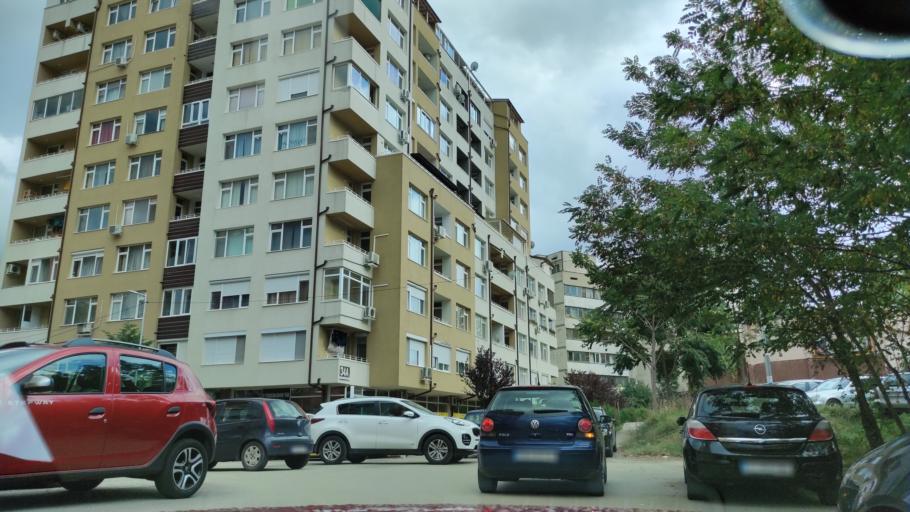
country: BG
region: Sofia-Capital
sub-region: Stolichna Obshtina
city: Sofia
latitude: 42.6557
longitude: 23.3436
